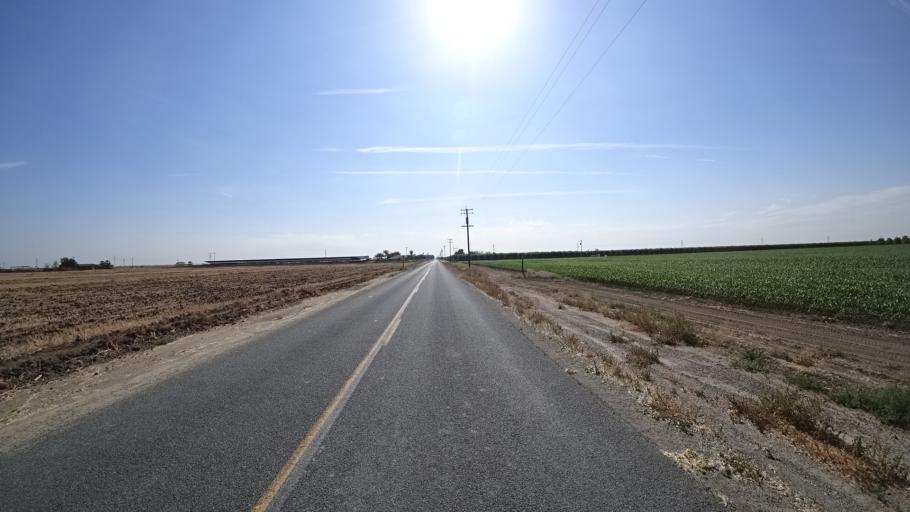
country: US
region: California
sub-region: Kings County
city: Home Garden
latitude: 36.2259
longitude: -119.5992
